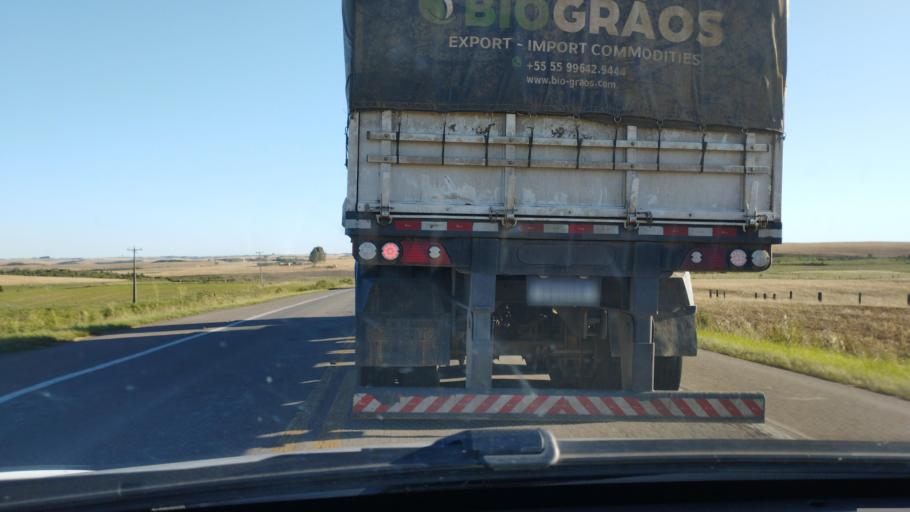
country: BR
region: Rio Grande do Sul
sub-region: Julio De Castilhos
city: Julio de Castilhos
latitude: -29.3841
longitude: -53.6698
